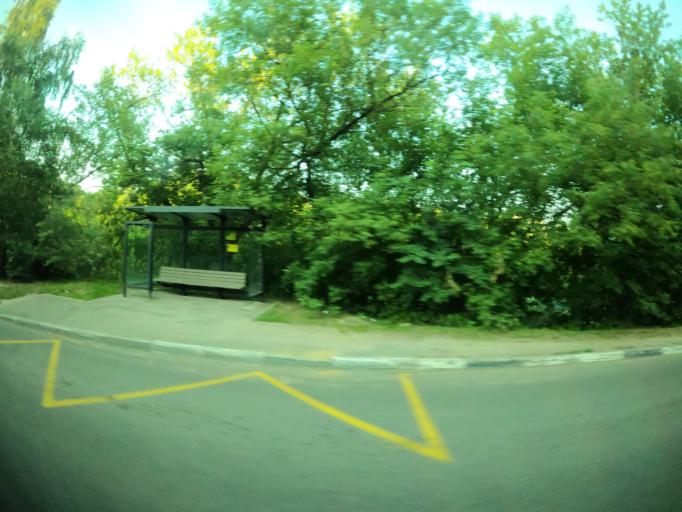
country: RU
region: Moskovskaya
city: Serpukhov
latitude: 54.9219
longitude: 37.4102
